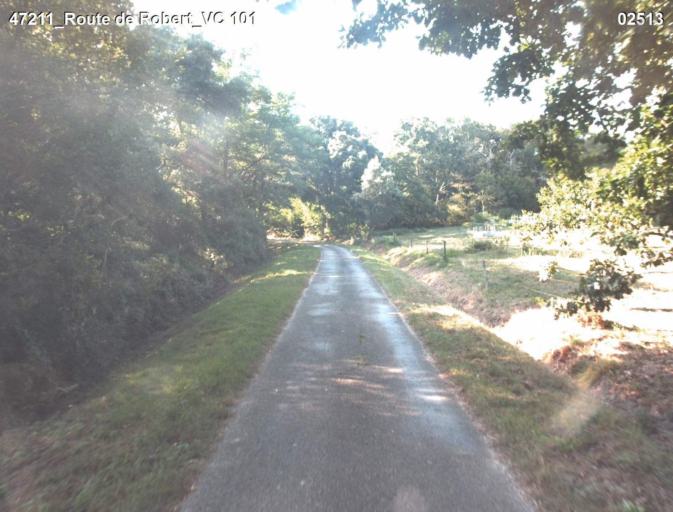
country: FR
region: Aquitaine
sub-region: Departement du Lot-et-Garonne
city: Mezin
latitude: 44.0528
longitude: 0.1810
